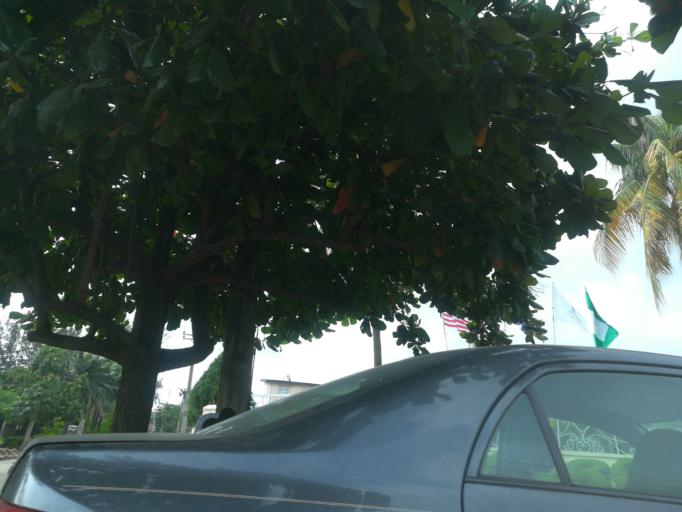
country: NG
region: Lagos
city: Oshodi
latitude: 6.5712
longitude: 3.3521
